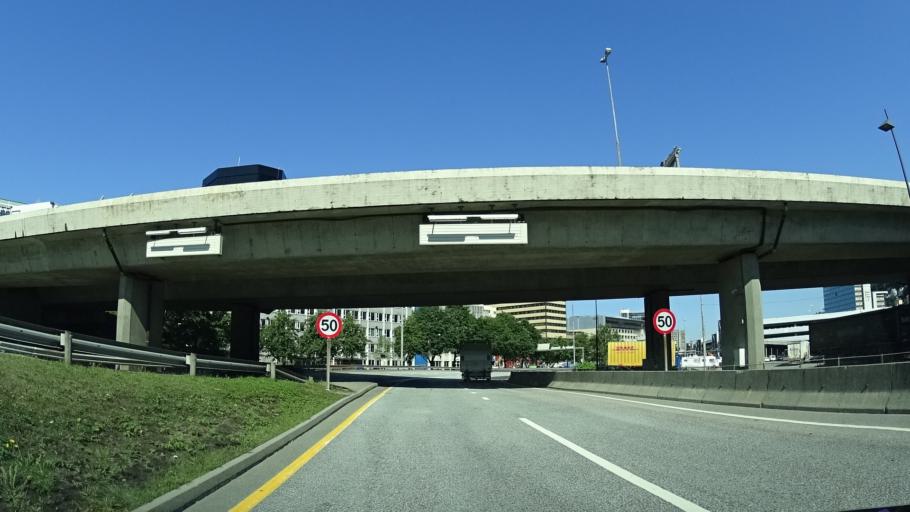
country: NO
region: Hordaland
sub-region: Bergen
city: Bergen
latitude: 60.3848
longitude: 5.3359
